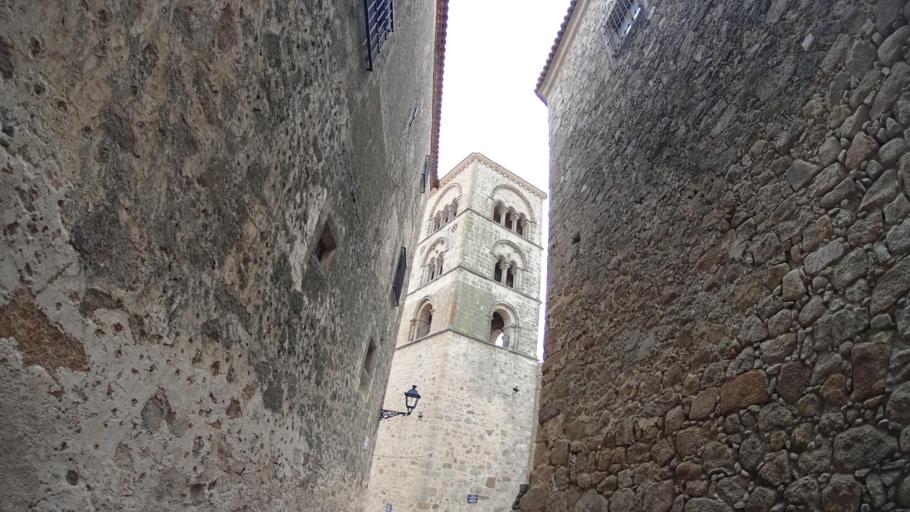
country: ES
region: Extremadura
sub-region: Provincia de Caceres
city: Trujillo
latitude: 39.4612
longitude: -5.8843
